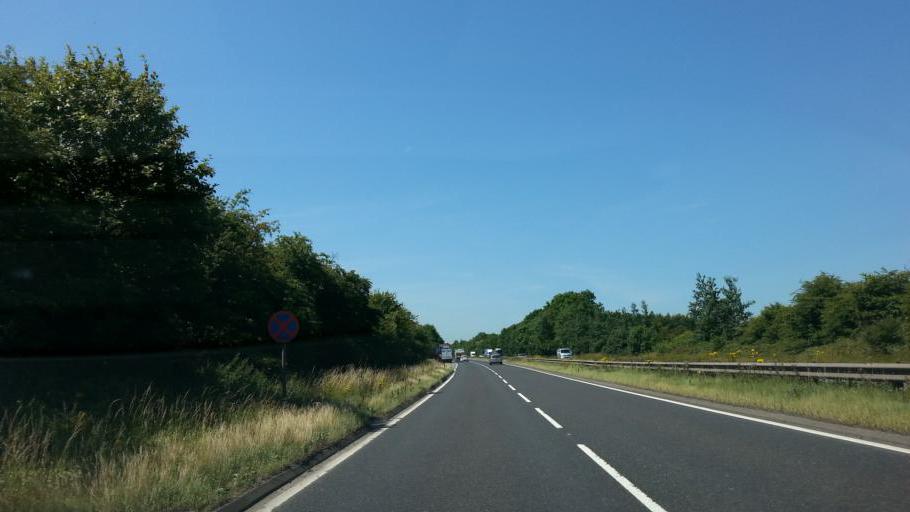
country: GB
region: England
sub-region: Derbyshire
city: Alfreton
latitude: 53.0928
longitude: -1.3570
